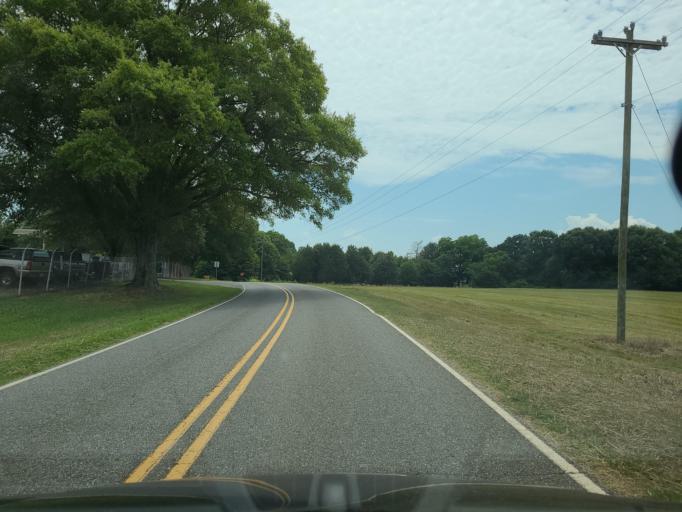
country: US
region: North Carolina
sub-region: Cleveland County
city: Boiling Springs
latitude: 35.2627
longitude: -81.6030
